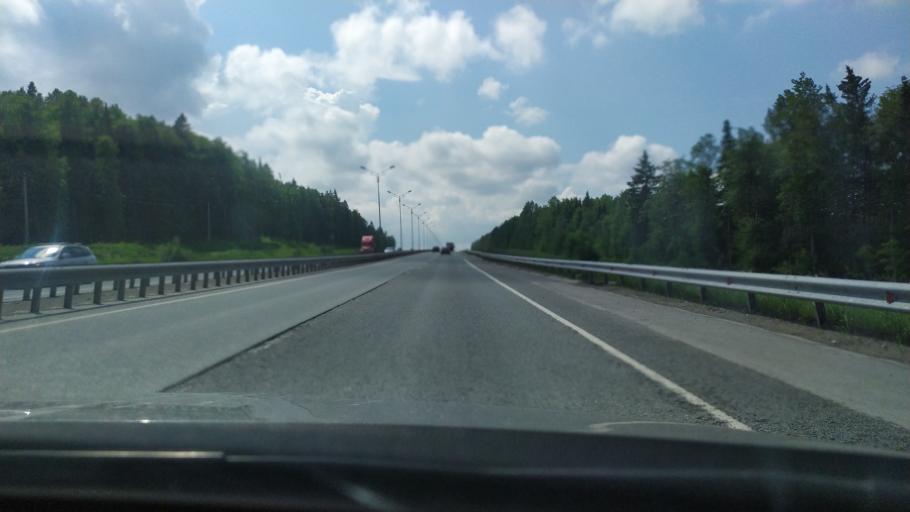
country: RU
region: Perm
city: Ferma
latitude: 58.0090
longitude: 56.3980
